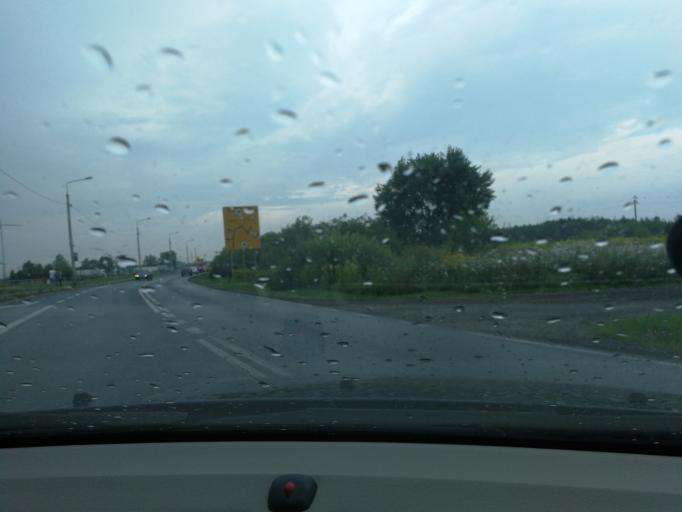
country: PL
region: Masovian Voivodeship
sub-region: Powiat zyrardowski
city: Mszczonow
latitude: 51.9777
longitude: 20.5289
